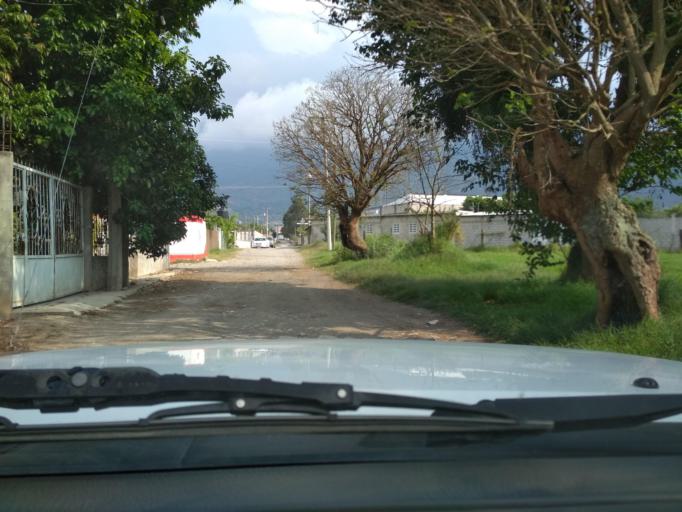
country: MX
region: Veracruz
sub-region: Acultzingo
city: Acatla
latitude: 18.7676
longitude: -97.2248
